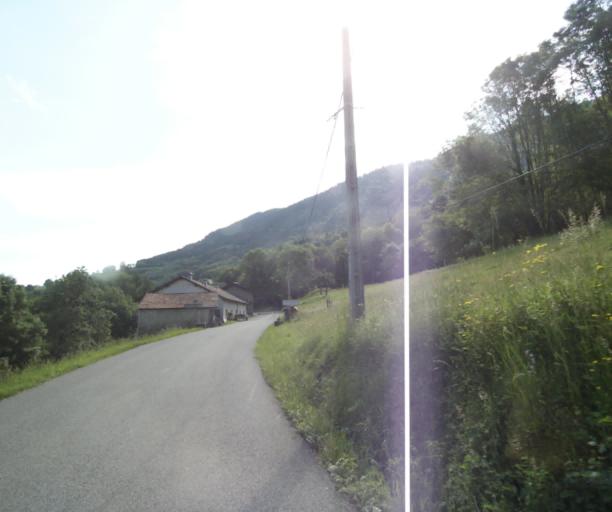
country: FR
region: Rhone-Alpes
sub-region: Departement de la Haute-Savoie
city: Lyaud
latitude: 46.3122
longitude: 6.5069
